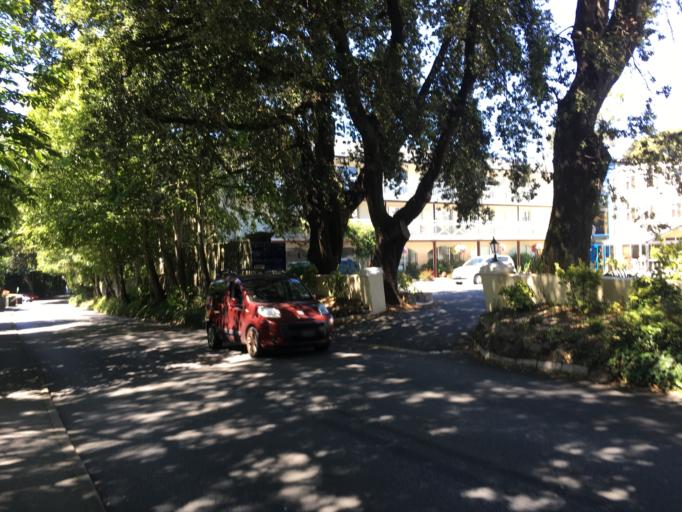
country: GG
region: St Peter Port
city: Saint Peter Port
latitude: 49.4571
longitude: -2.5515
